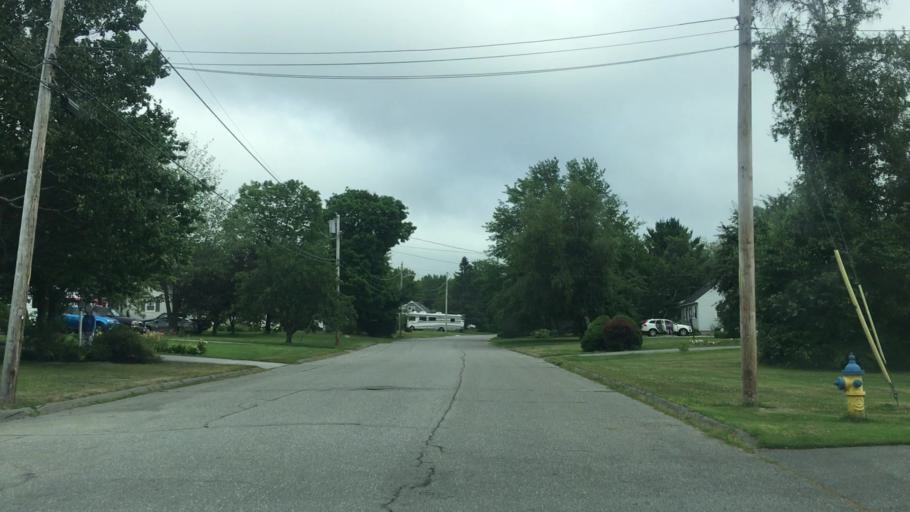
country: US
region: Maine
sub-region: Penobscot County
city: Brewer
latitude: 44.7730
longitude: -68.7686
